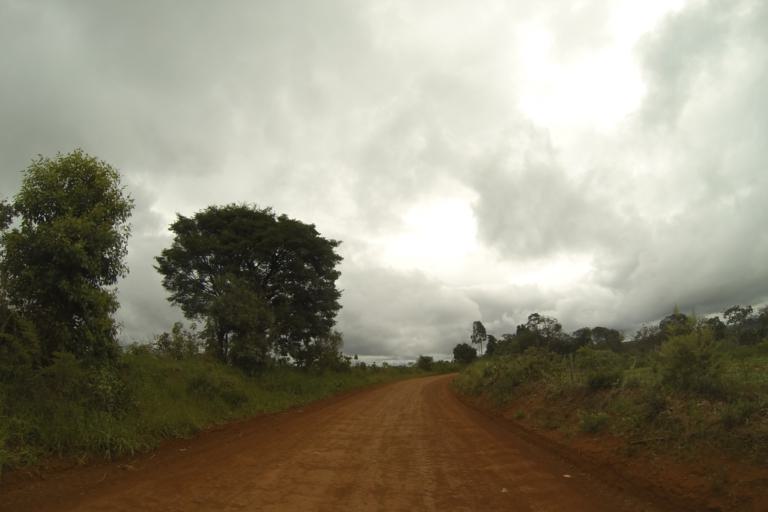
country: BR
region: Minas Gerais
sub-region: Campos Altos
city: Campos Altos
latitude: -19.8563
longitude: -46.3152
